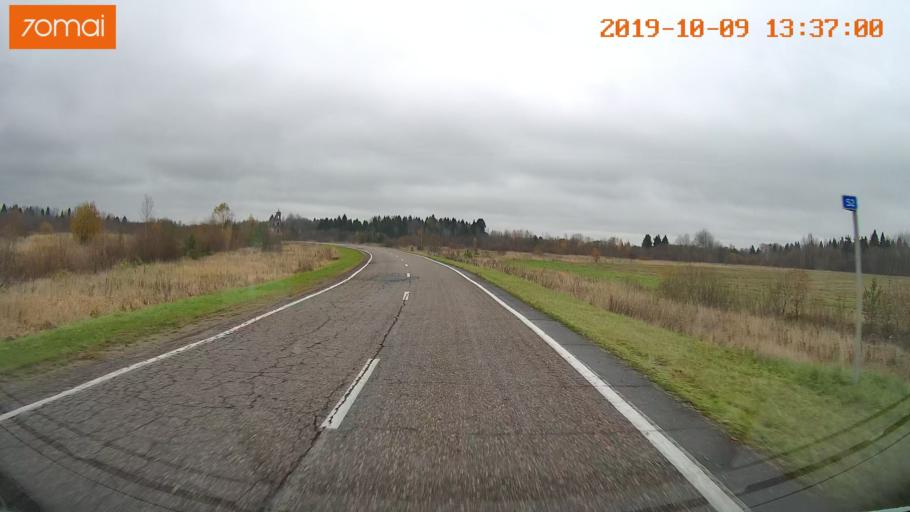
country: RU
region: Jaroslavl
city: Lyubim
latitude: 58.3390
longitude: 41.1101
